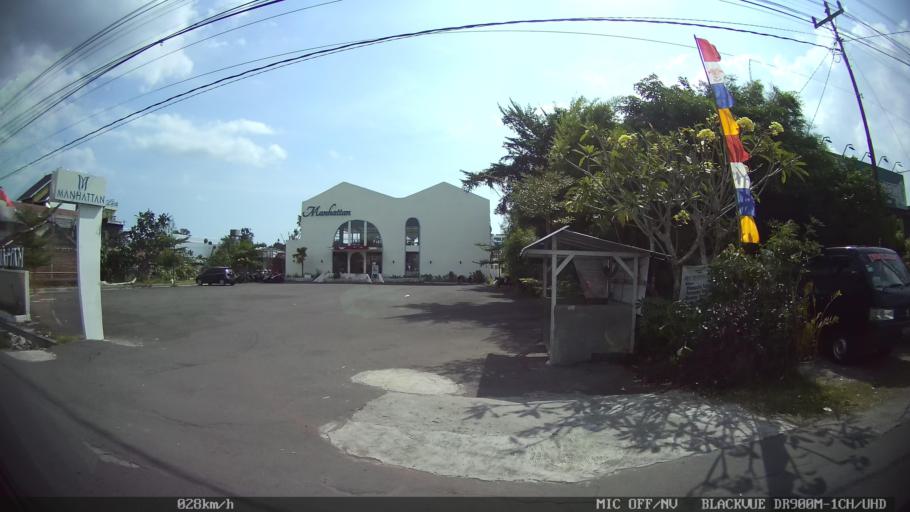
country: ID
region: Daerah Istimewa Yogyakarta
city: Kasihan
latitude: -7.8185
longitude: 110.3282
